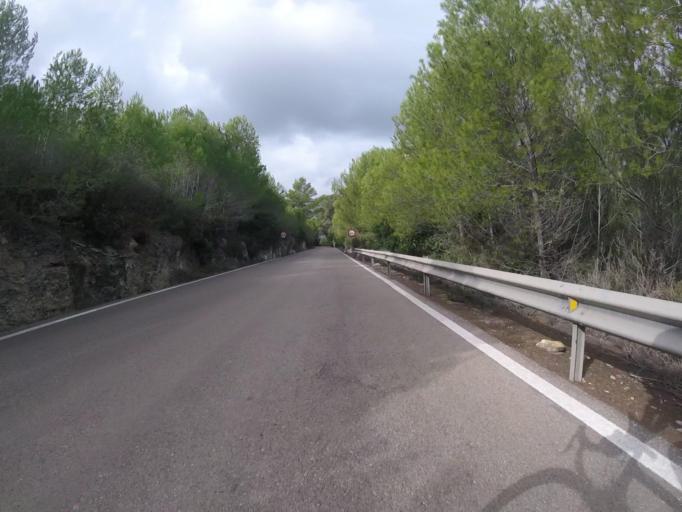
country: ES
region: Valencia
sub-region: Provincia de Castello
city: Orpesa/Oropesa del Mar
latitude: 40.1436
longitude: 0.1069
